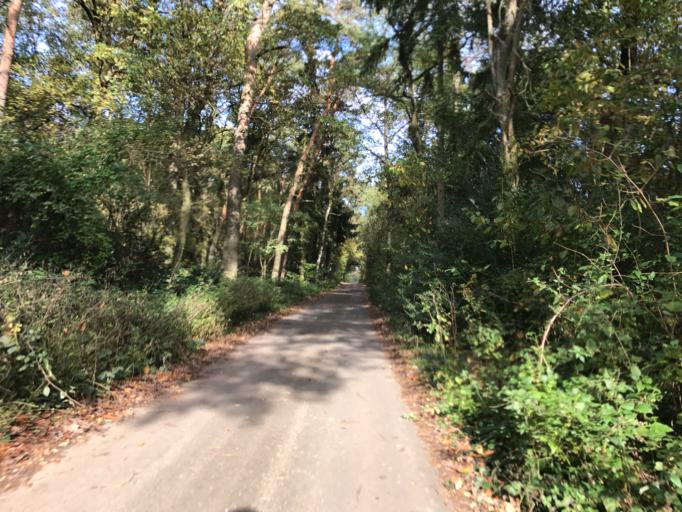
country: DE
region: Rheinland-Pfalz
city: Ockenheim
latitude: 49.9238
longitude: 7.9839
